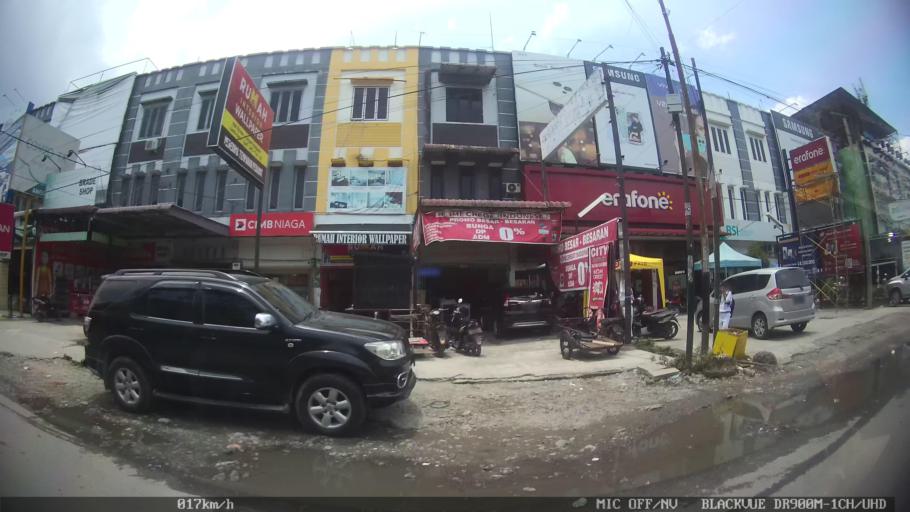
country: ID
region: North Sumatra
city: Labuhan Deli
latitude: 3.7029
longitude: 98.6583
